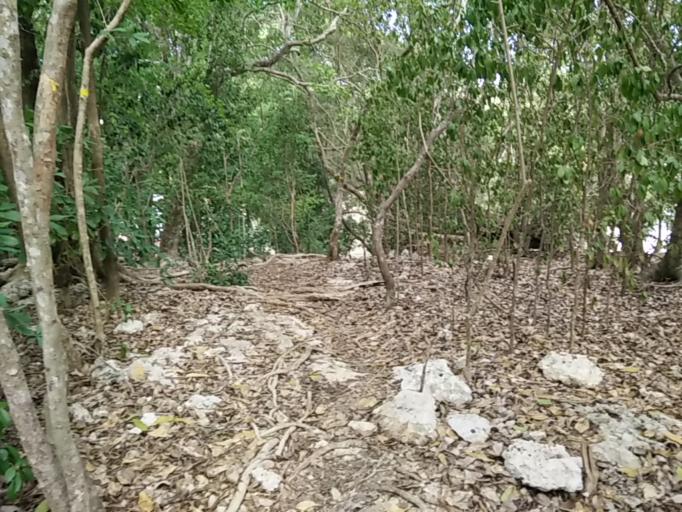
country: GP
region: Guadeloupe
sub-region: Guadeloupe
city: Sainte-Anne
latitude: 16.2102
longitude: -61.4262
